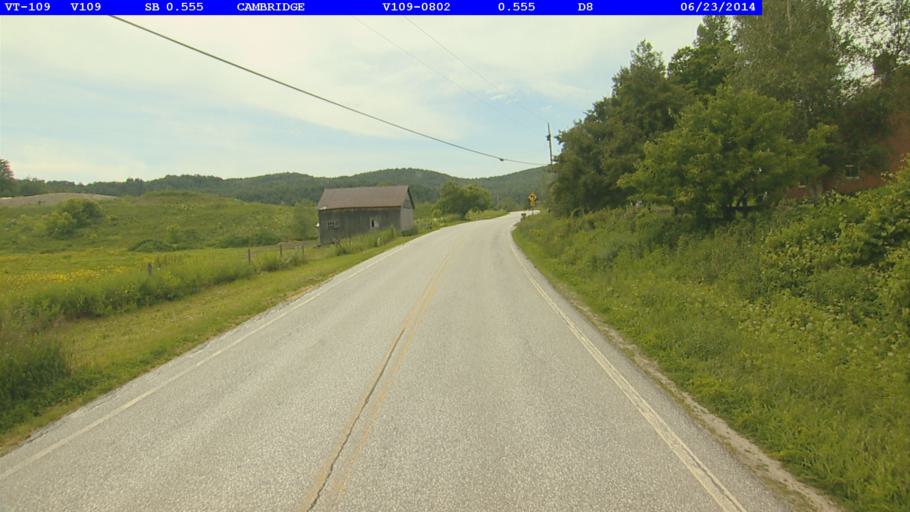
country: US
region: Vermont
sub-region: Lamoille County
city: Johnson
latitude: 44.6535
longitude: -72.8174
